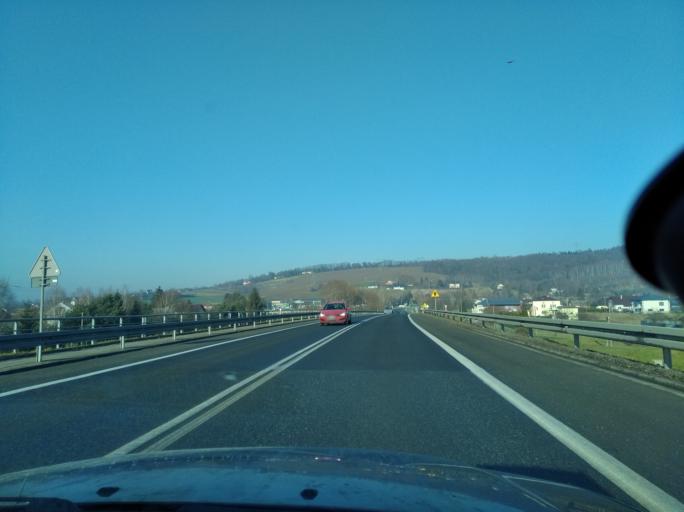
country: PL
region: Subcarpathian Voivodeship
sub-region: Powiat strzyzowski
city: Babica
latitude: 49.9302
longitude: 21.8724
